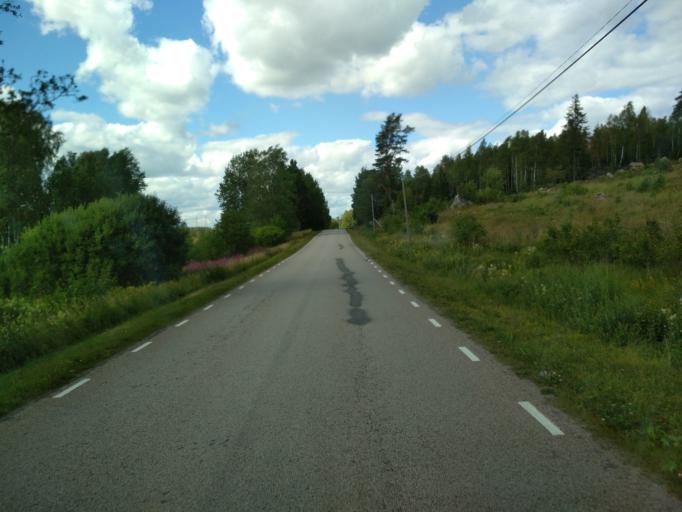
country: SE
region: Uppsala
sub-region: Enkopings Kommun
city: Orsundsbro
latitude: 59.7781
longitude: 17.2127
